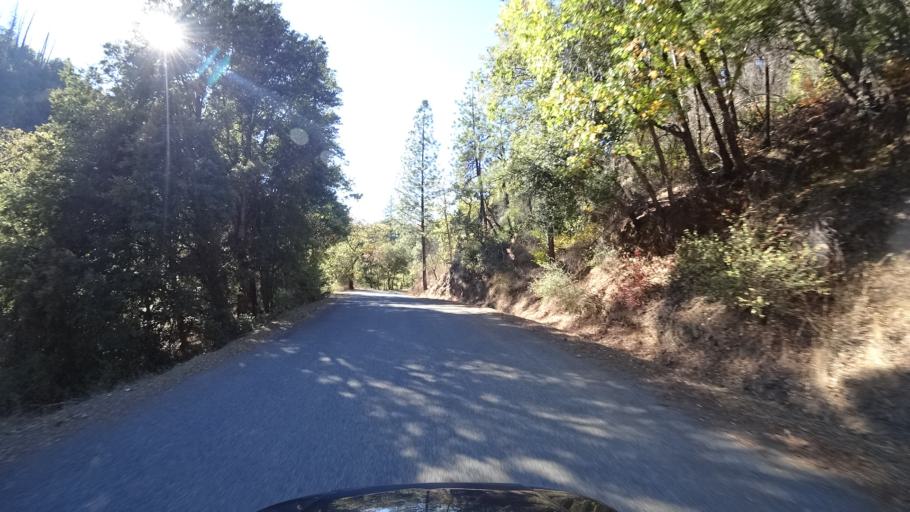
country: US
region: California
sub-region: Humboldt County
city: Willow Creek
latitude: 41.2817
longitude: -123.2576
